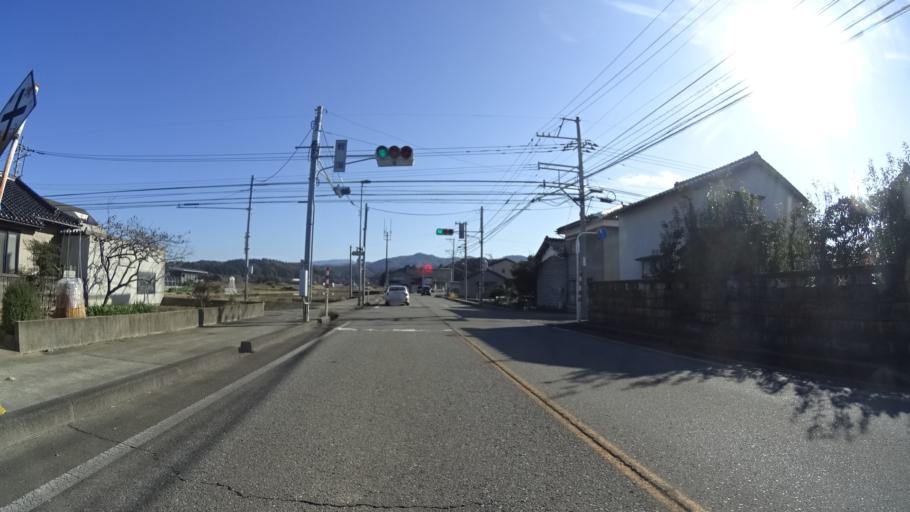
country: JP
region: Ishikawa
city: Komatsu
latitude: 36.3999
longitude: 136.5119
